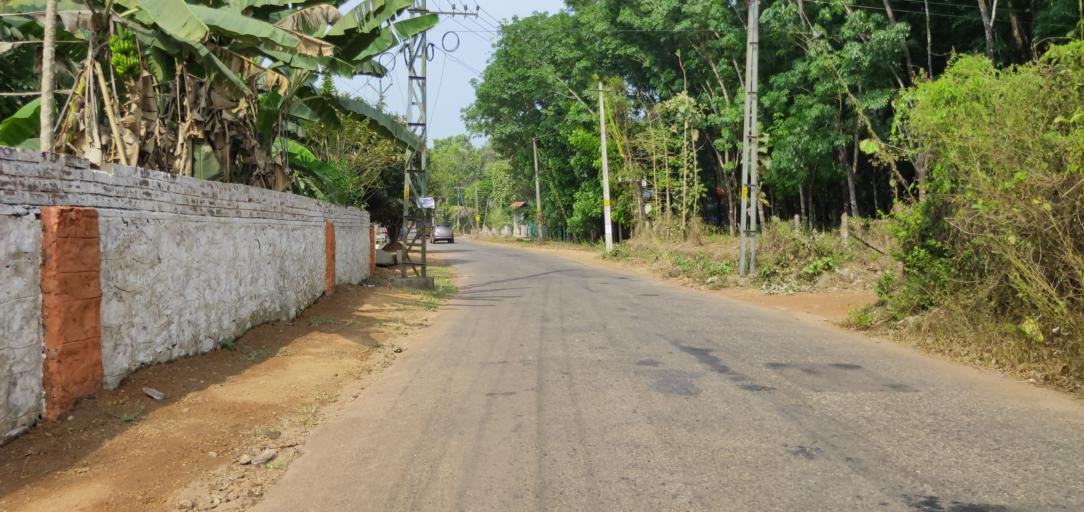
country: IN
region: Kerala
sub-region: Malappuram
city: Manjeri
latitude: 11.2305
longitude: 76.2773
